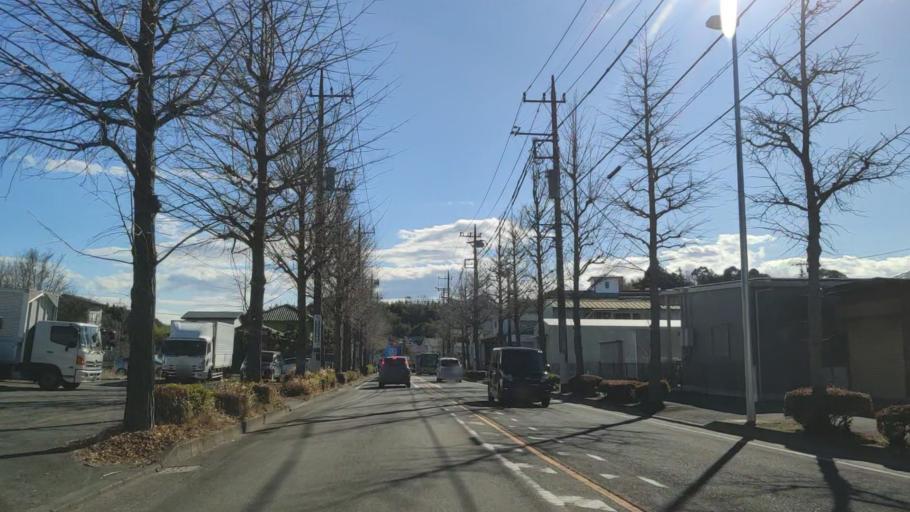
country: JP
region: Kanagawa
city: Minami-rinkan
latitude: 35.4992
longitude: 139.5001
